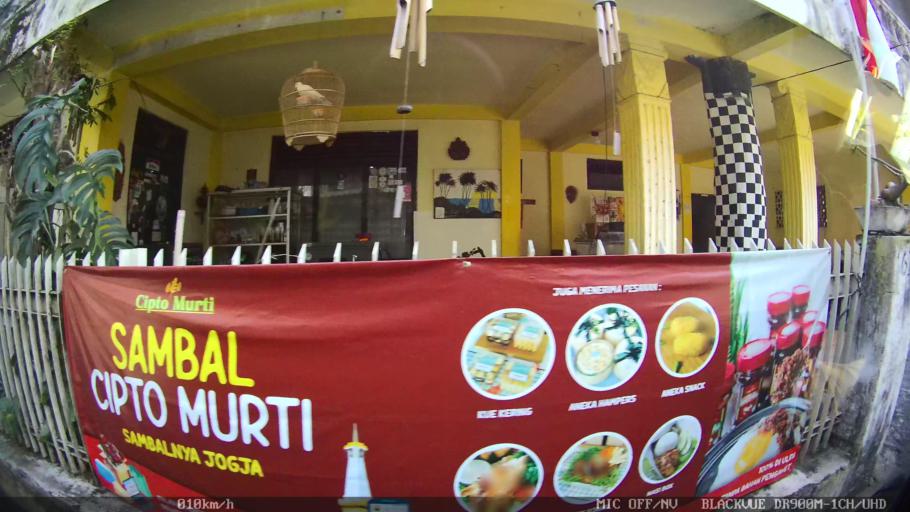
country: ID
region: Daerah Istimewa Yogyakarta
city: Yogyakarta
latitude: -7.8064
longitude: 110.3764
